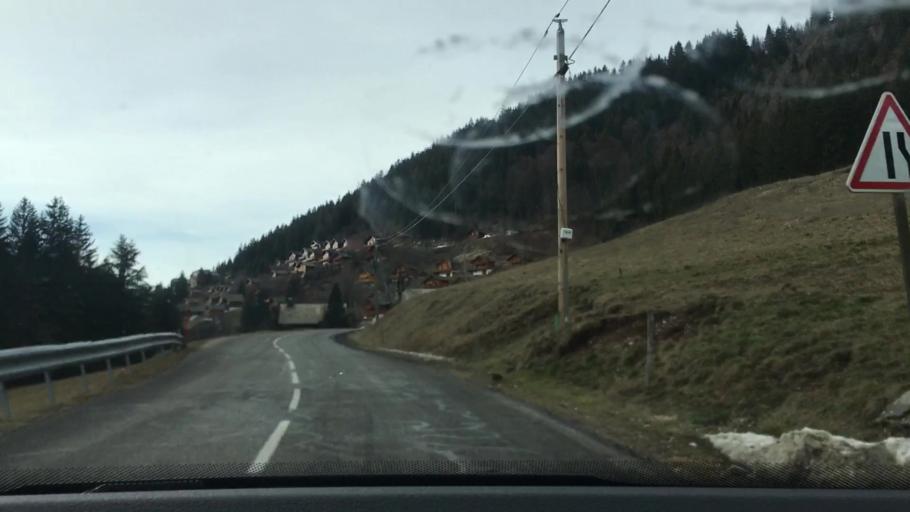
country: FR
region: Rhone-Alpes
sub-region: Departement de la Haute-Savoie
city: Abondance
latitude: 46.2869
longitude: 6.6552
